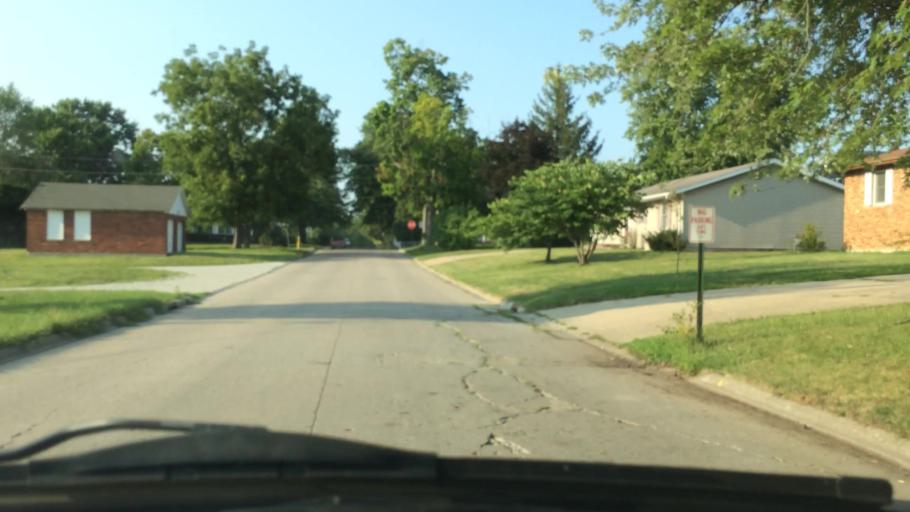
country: US
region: Iowa
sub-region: Henry County
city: Mount Pleasant
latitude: 40.9664
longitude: -91.5602
